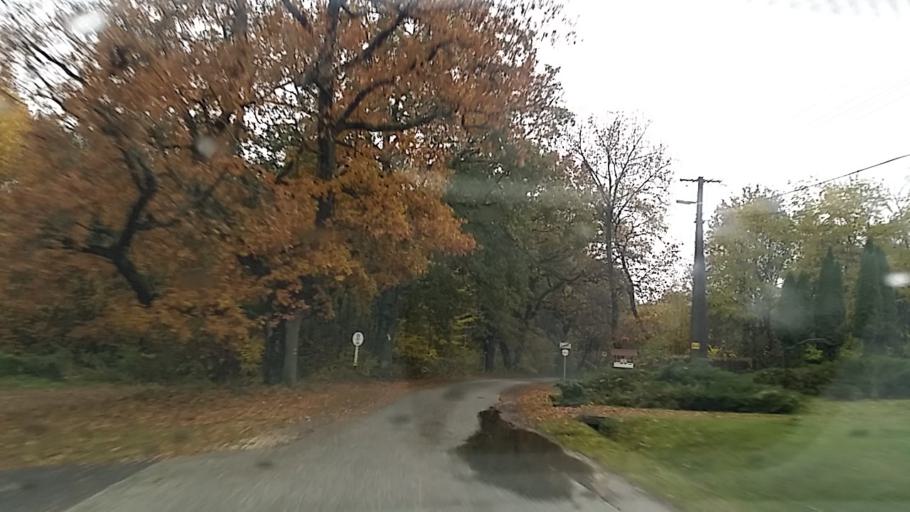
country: HU
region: Borsod-Abauj-Zemplen
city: Sarospatak
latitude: 48.4566
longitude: 21.4783
